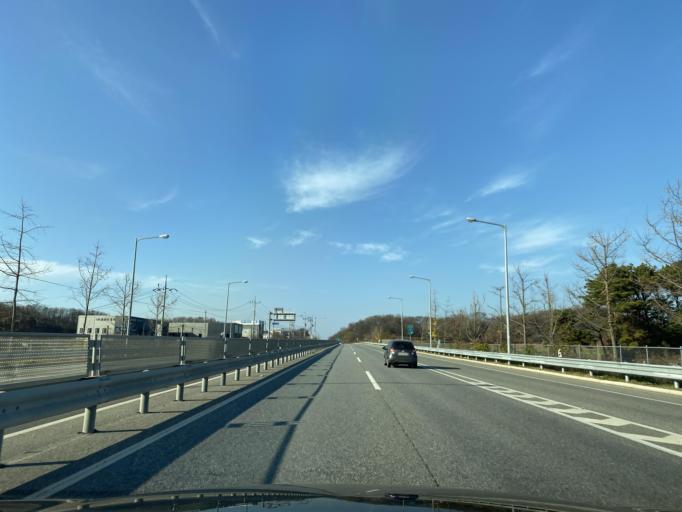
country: KR
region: Chungcheongnam-do
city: Asan
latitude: 36.7683
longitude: 126.9467
